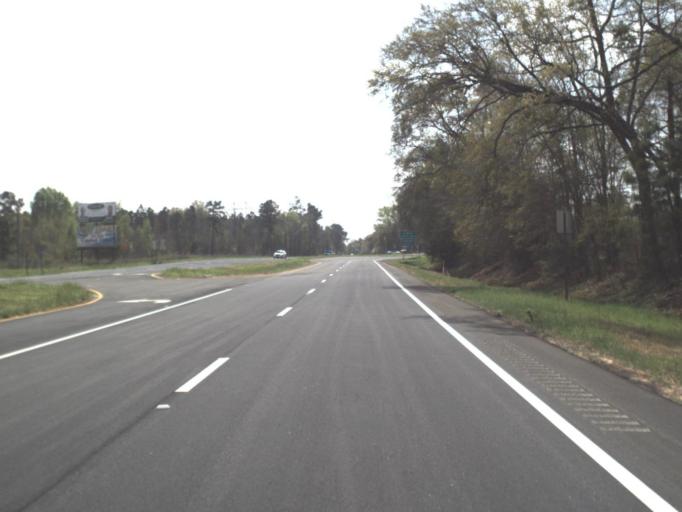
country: US
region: Florida
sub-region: Gadsden County
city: Havana
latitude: 30.6912
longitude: -84.3816
